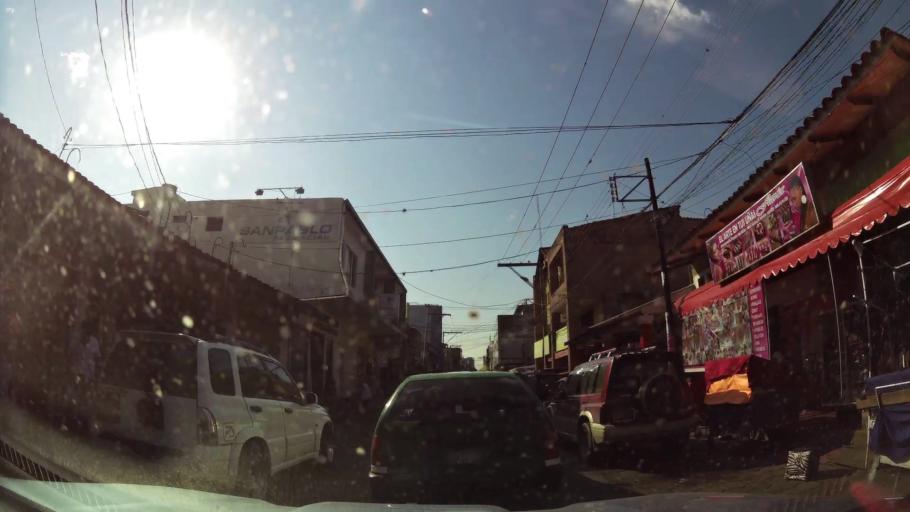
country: BO
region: Santa Cruz
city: Santa Cruz de la Sierra
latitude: -17.7797
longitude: -63.1778
